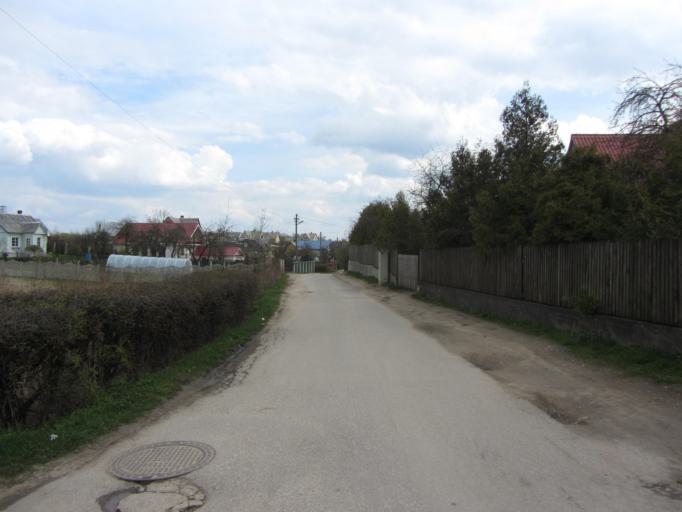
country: LT
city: Lentvaris
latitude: 54.6482
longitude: 25.0613
